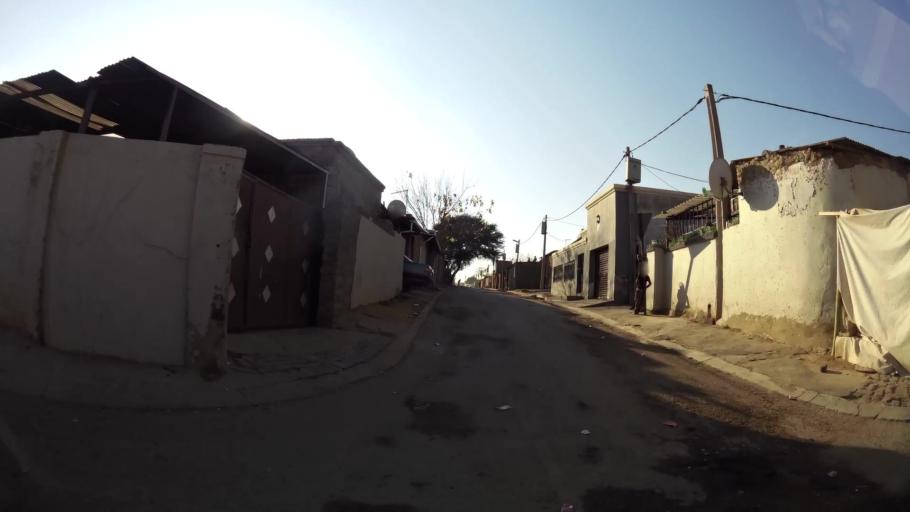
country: ZA
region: Gauteng
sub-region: City of Johannesburg Metropolitan Municipality
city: Modderfontein
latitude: -26.0875
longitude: 28.1127
